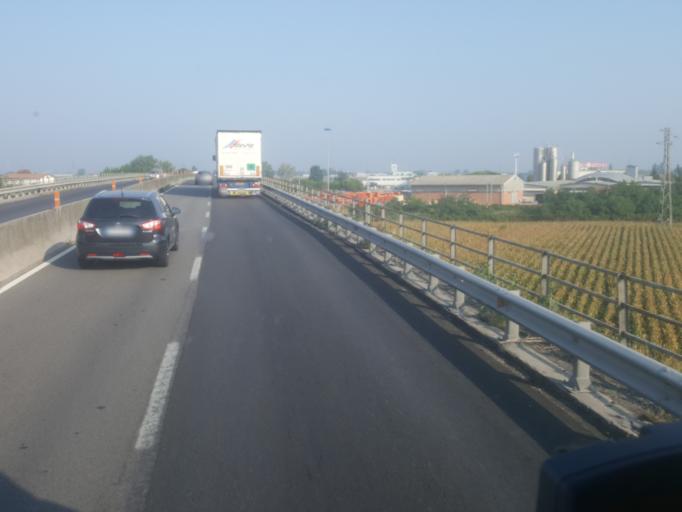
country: IT
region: Emilia-Romagna
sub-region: Provincia di Ravenna
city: Fornace Zarattini
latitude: 44.4205
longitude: 12.1649
